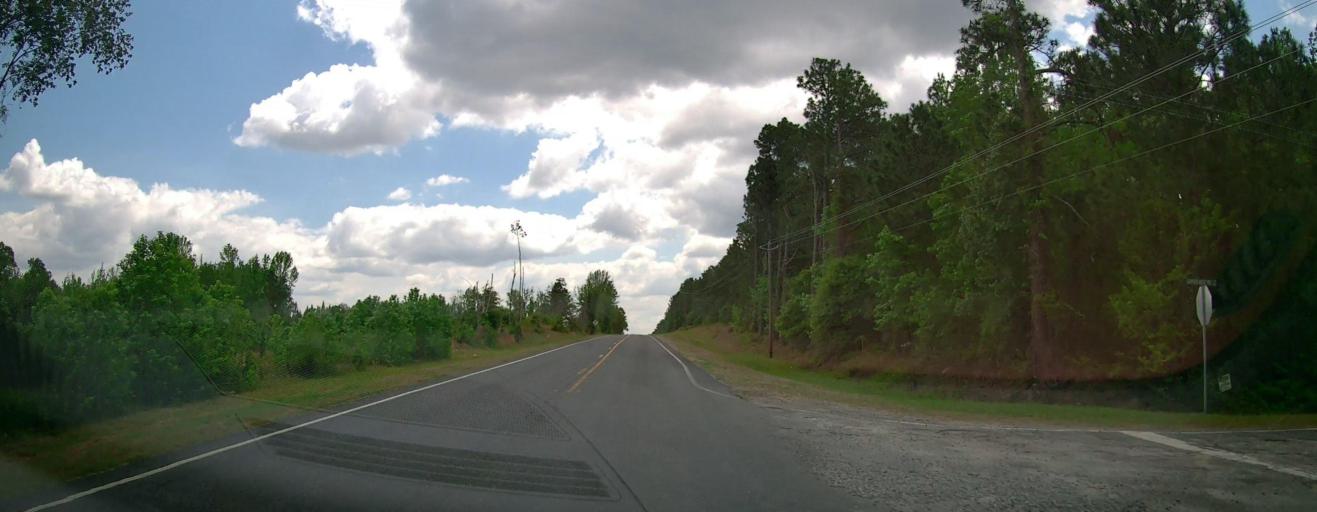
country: US
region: Georgia
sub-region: Treutlen County
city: Soperton
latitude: 32.4679
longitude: -82.6025
